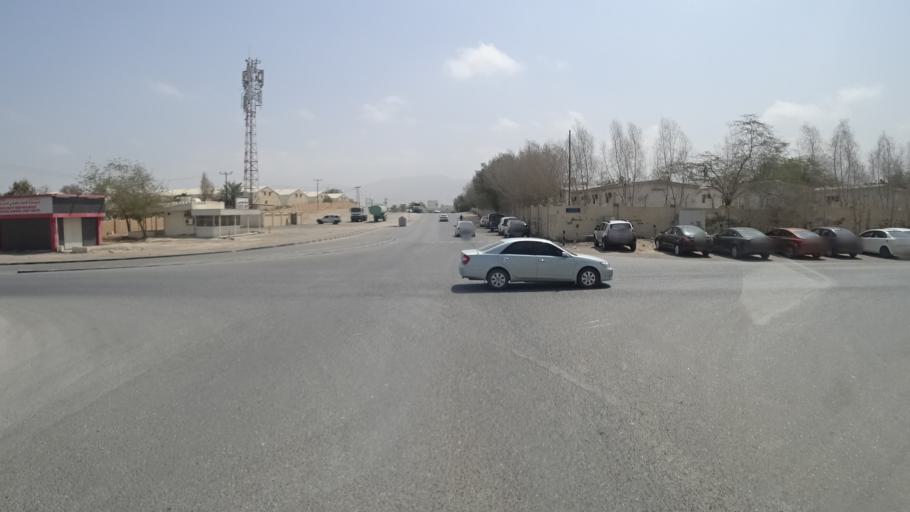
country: OM
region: Muhafazat Masqat
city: Bawshar
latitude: 23.5758
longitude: 58.3554
